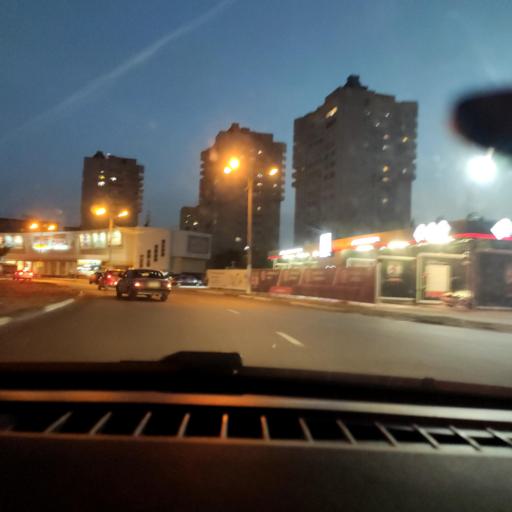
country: RU
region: Voronezj
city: Podgornoye
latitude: 51.7169
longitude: 39.1710
